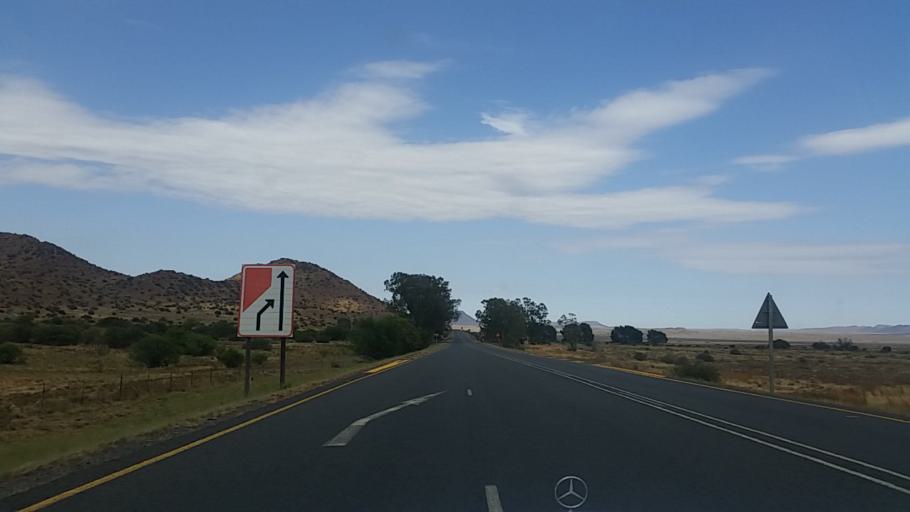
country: ZA
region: Northern Cape
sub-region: Pixley ka Seme District Municipality
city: Colesberg
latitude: -30.6462
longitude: 25.2134
